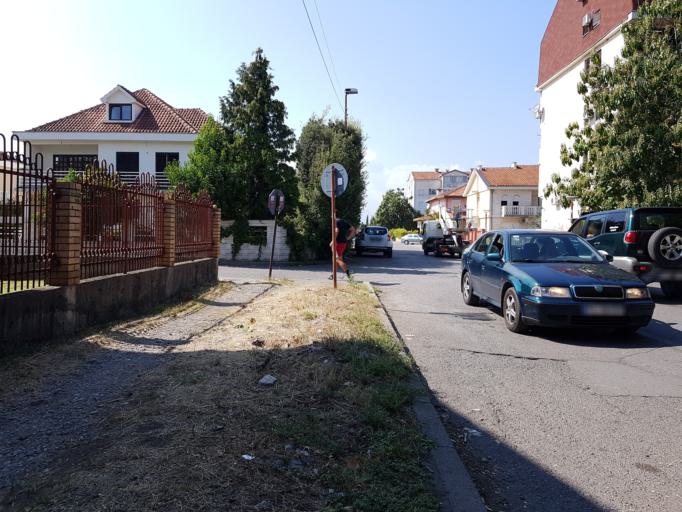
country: ME
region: Podgorica
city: Podgorica
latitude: 42.4334
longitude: 19.2762
